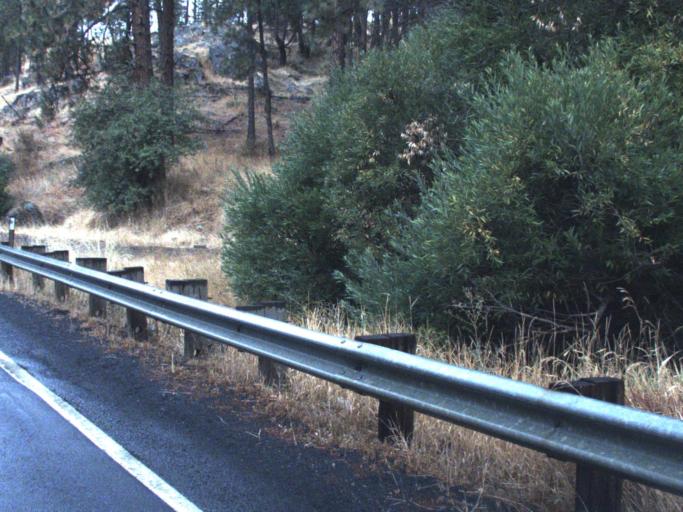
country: US
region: Washington
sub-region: Spokane County
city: Medical Lake
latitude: 47.7390
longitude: -117.8753
